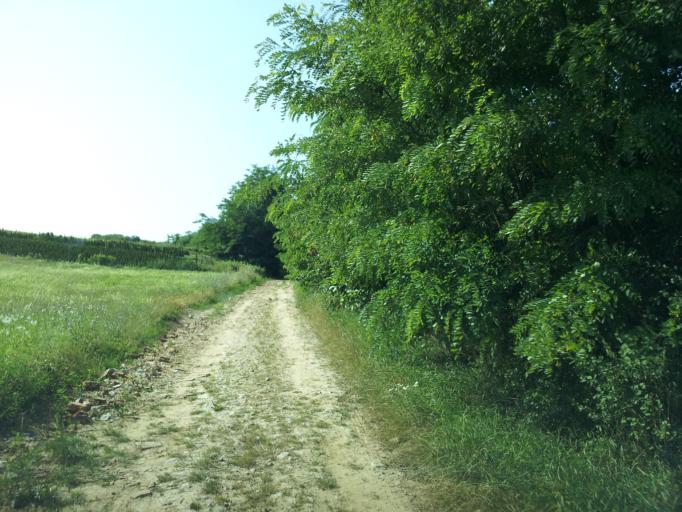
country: HU
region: Zala
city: Cserszegtomaj
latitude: 46.8479
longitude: 17.2129
